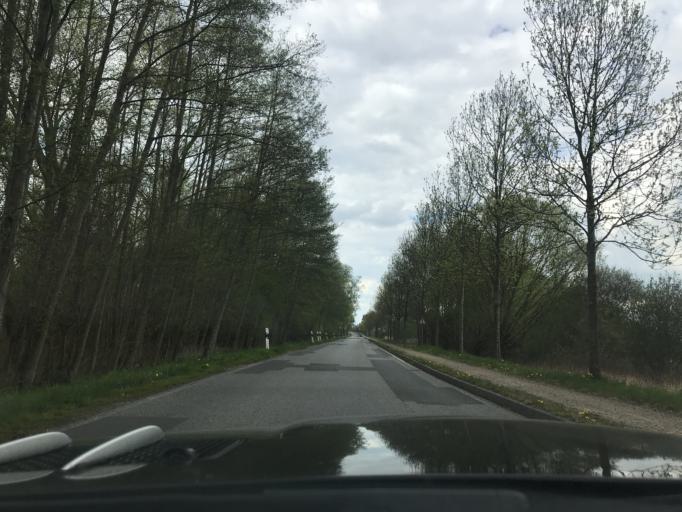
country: DE
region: Schleswig-Holstein
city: Gross Gronau
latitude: 53.7786
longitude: 10.7696
